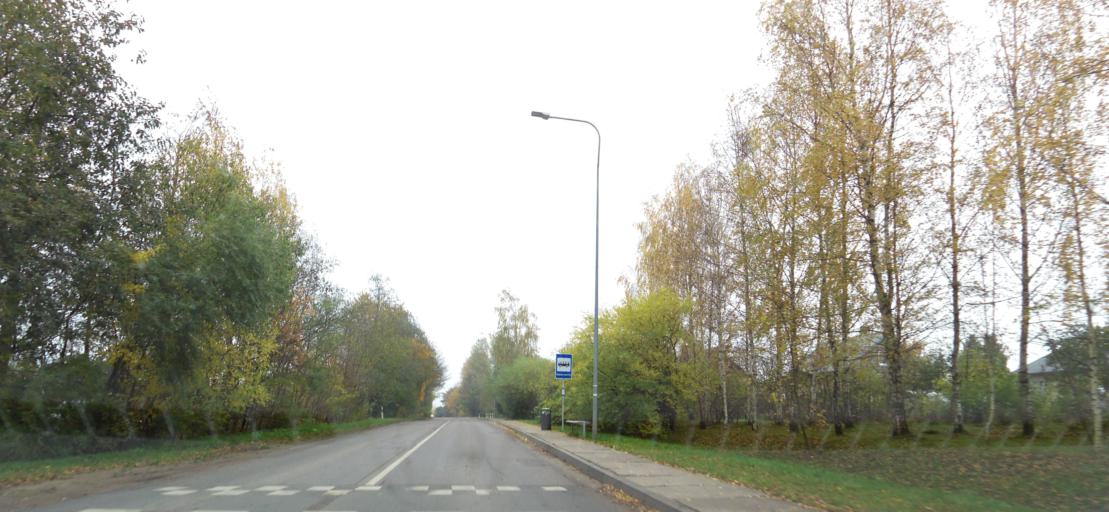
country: LT
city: Skaidiskes
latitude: 54.6590
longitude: 25.3647
